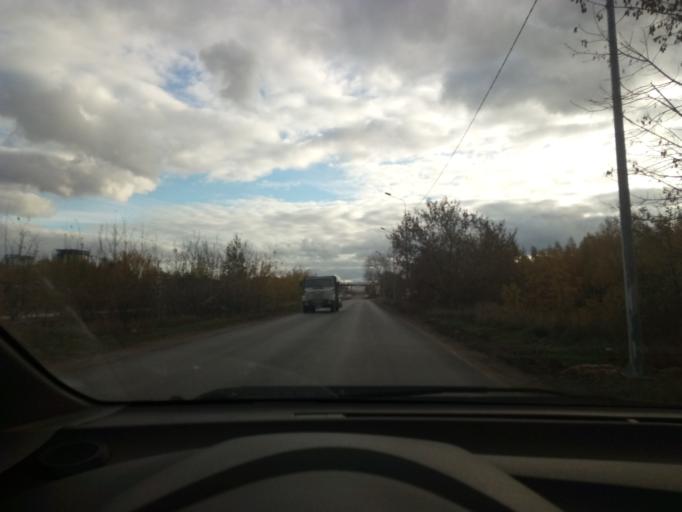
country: RU
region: Tatarstan
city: Staroye Arakchino
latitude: 55.8836
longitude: 48.9761
